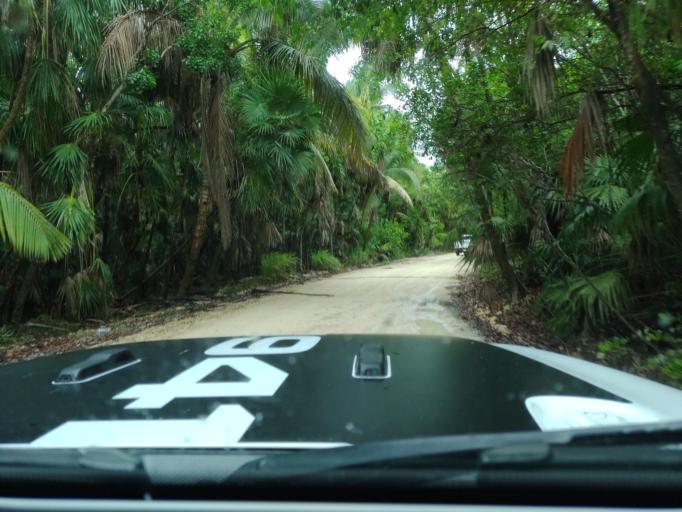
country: MX
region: Quintana Roo
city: Tulum
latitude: 20.0575
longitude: -87.4809
